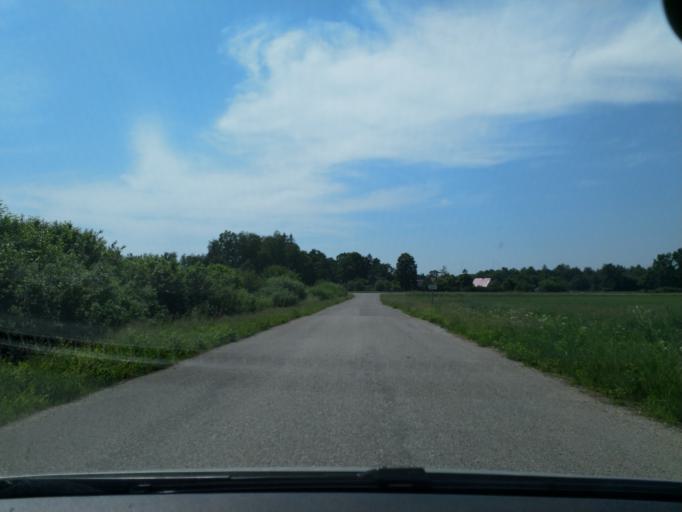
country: LV
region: Kuldigas Rajons
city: Kuldiga
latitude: 56.9539
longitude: 22.0124
